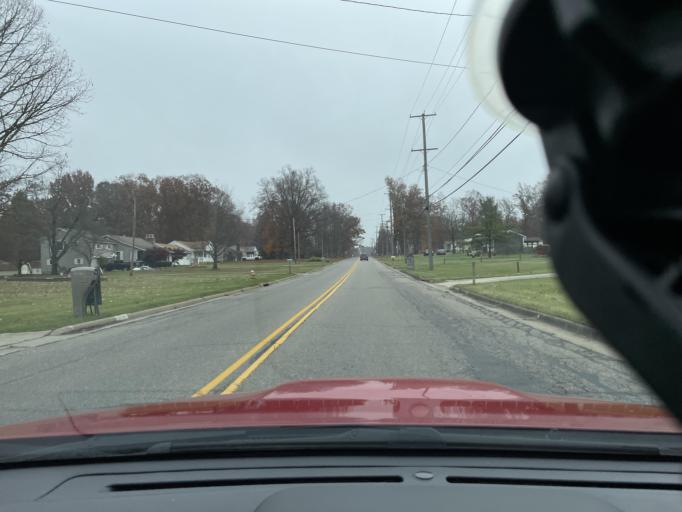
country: US
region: Ohio
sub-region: Mahoning County
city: Austintown
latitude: 41.1058
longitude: -80.7528
